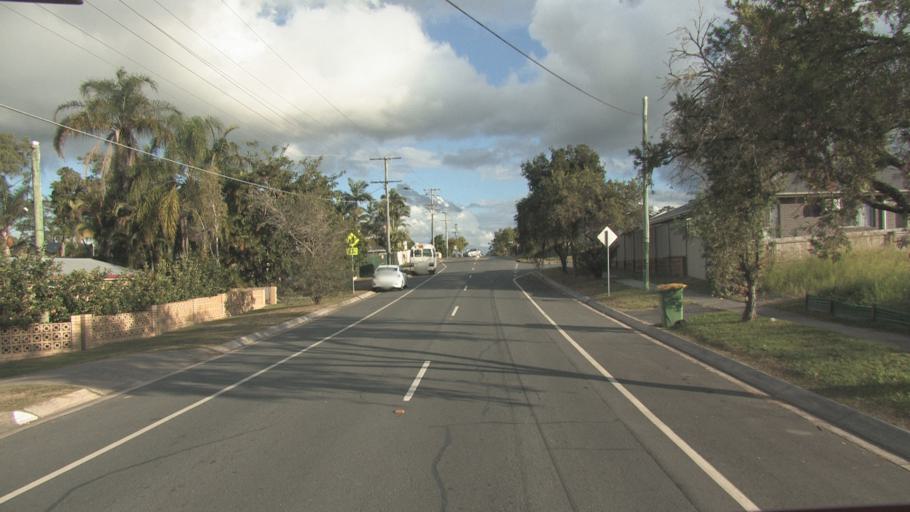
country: AU
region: Queensland
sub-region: Logan
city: Park Ridge South
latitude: -27.6858
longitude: 153.0232
